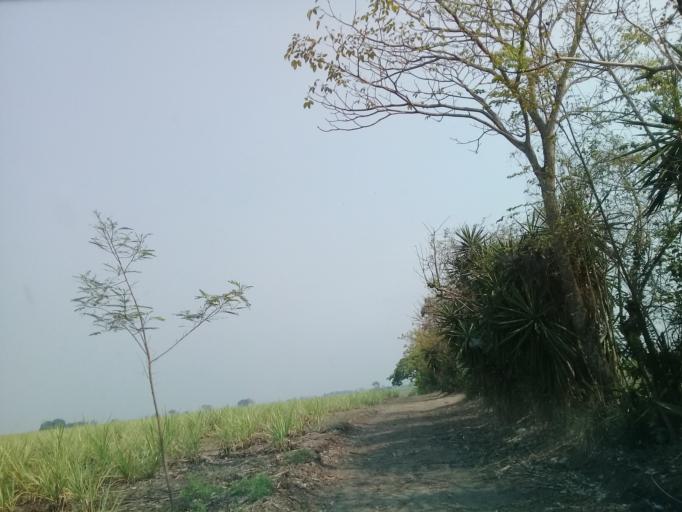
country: MX
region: Oaxaca
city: Acatlan de Perez Figueroa
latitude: 18.6087
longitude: -96.5727
